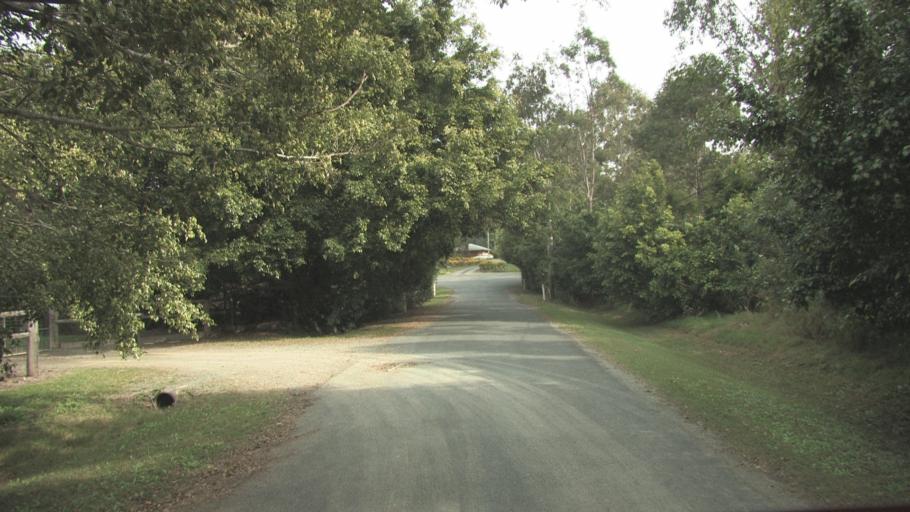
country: AU
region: Queensland
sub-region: Logan
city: Waterford West
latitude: -27.7332
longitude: 153.1359
